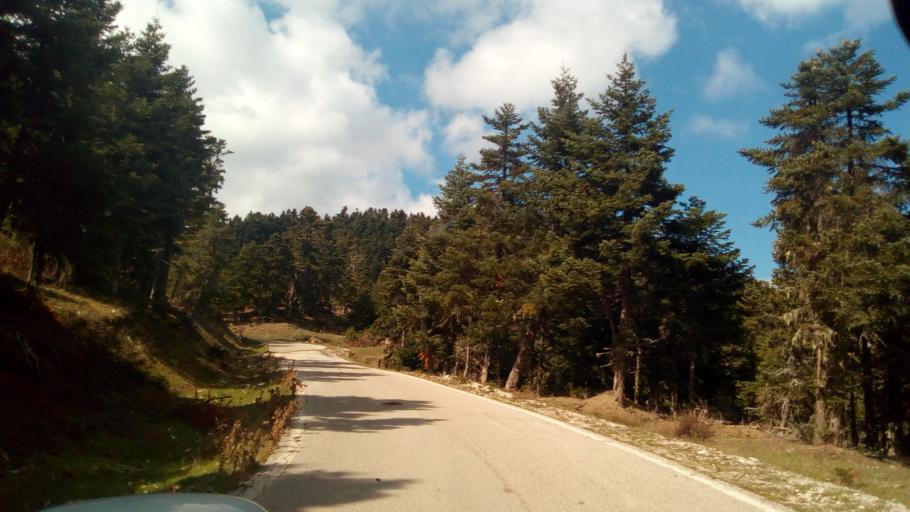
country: GR
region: West Greece
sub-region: Nomos Aitolias kai Akarnanias
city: Nafpaktos
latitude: 38.6398
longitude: 21.9411
